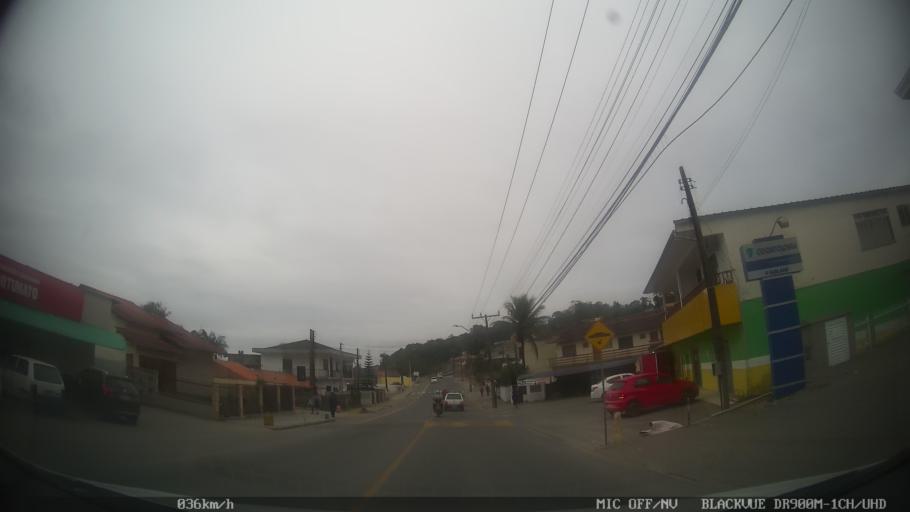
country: BR
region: Santa Catarina
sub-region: Joinville
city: Joinville
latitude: -26.3498
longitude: -48.8186
